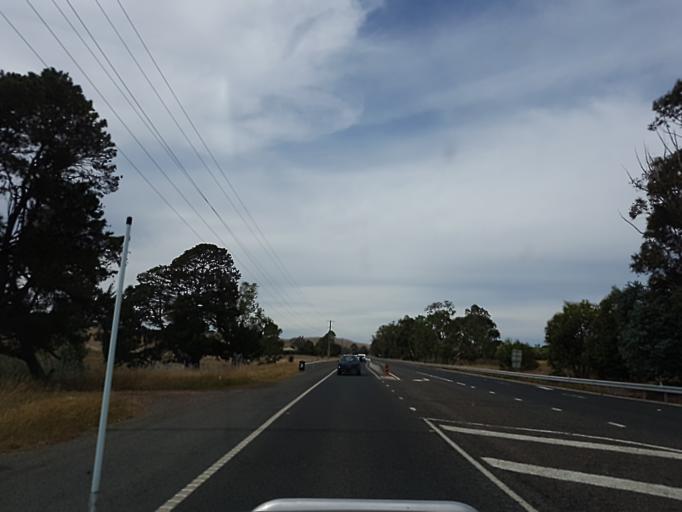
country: AU
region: Victoria
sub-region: Murrindindi
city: Alexandra
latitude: -37.2068
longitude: 145.4586
